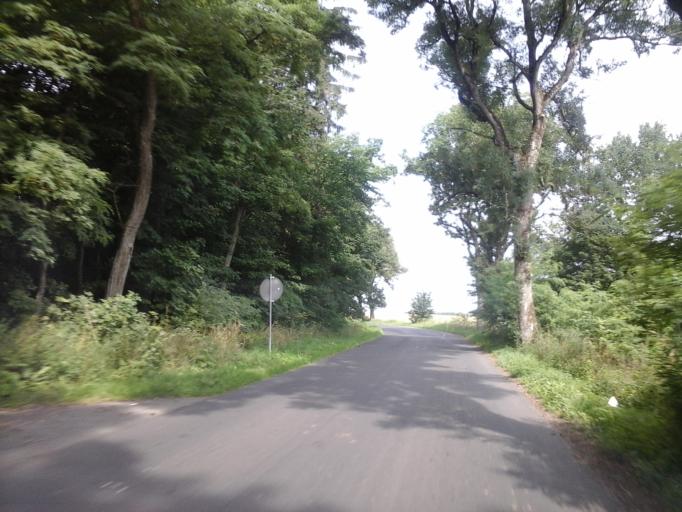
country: PL
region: West Pomeranian Voivodeship
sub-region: Powiat choszczenski
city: Recz
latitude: 53.2487
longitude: 15.6065
